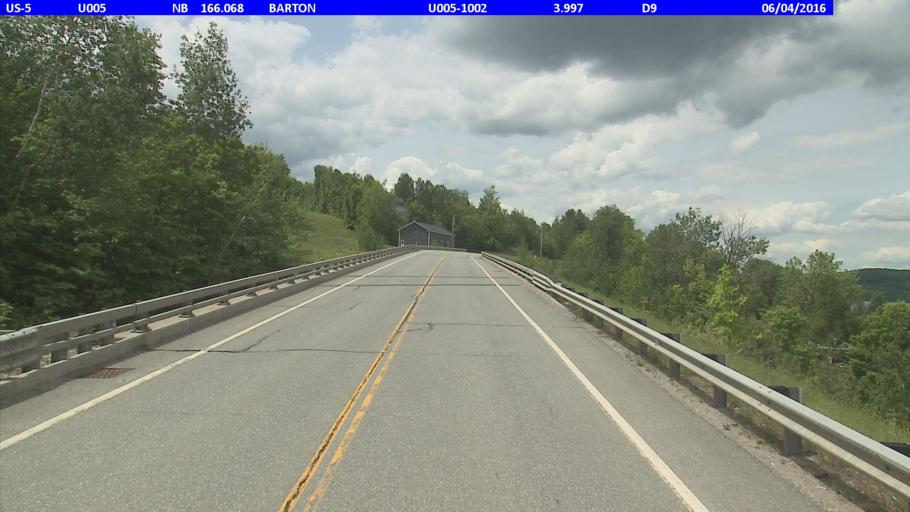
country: US
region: Vermont
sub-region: Orleans County
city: Newport
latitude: 44.7318
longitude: -72.1599
